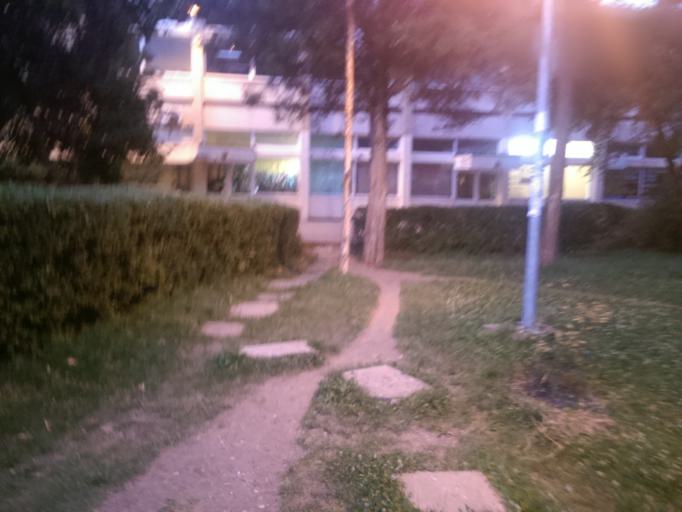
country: RO
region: Cluj
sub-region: Municipiul Cluj-Napoca
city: Cluj-Napoca
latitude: 46.7670
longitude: 23.6241
